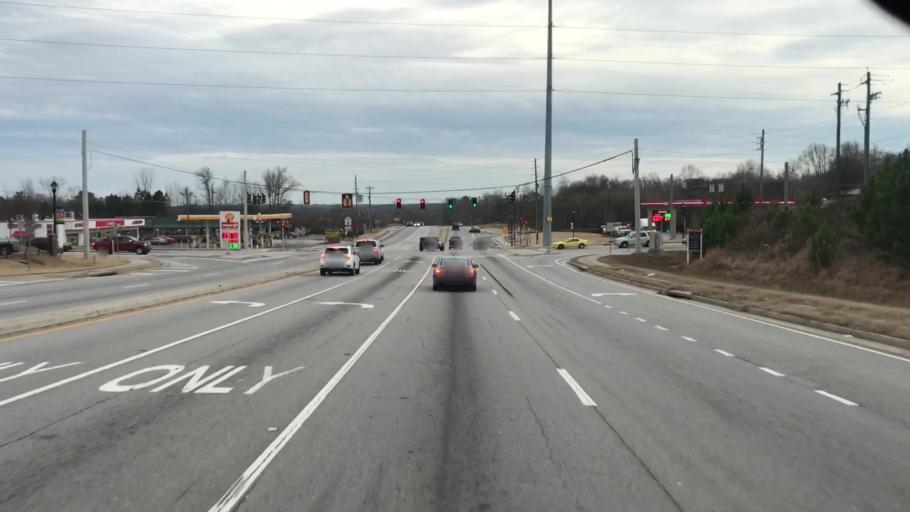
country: US
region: Georgia
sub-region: Jackson County
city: Hoschton
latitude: 34.0949
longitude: -83.8104
